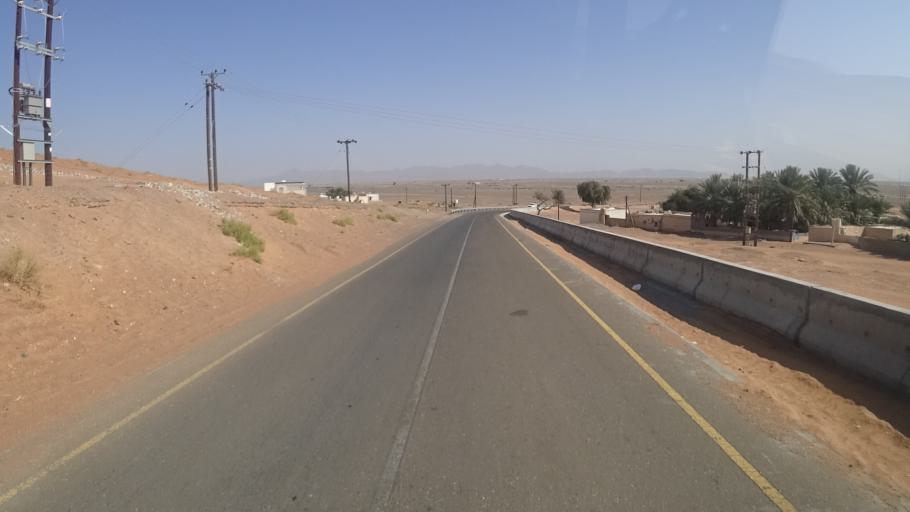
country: OM
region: Ash Sharqiyah
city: Al Qabil
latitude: 22.4992
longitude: 58.7163
